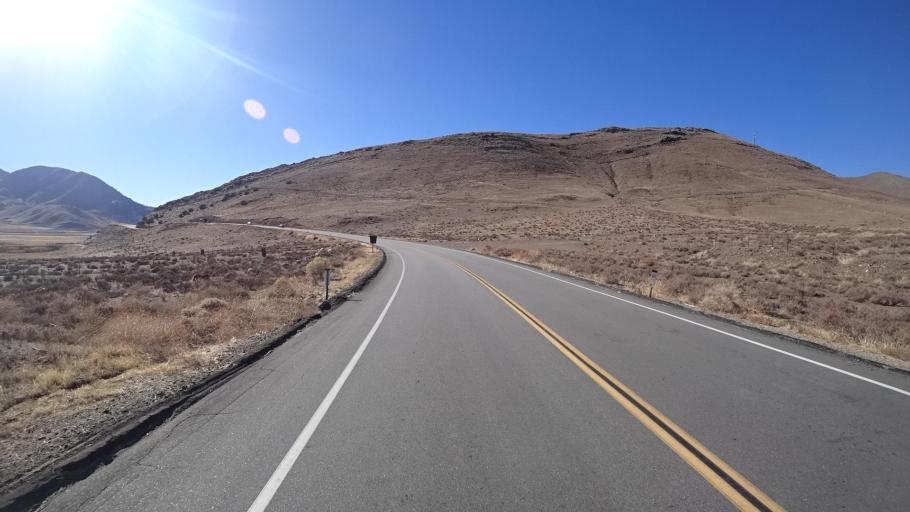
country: US
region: California
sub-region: Kern County
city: Wofford Heights
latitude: 35.6804
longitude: -118.4114
